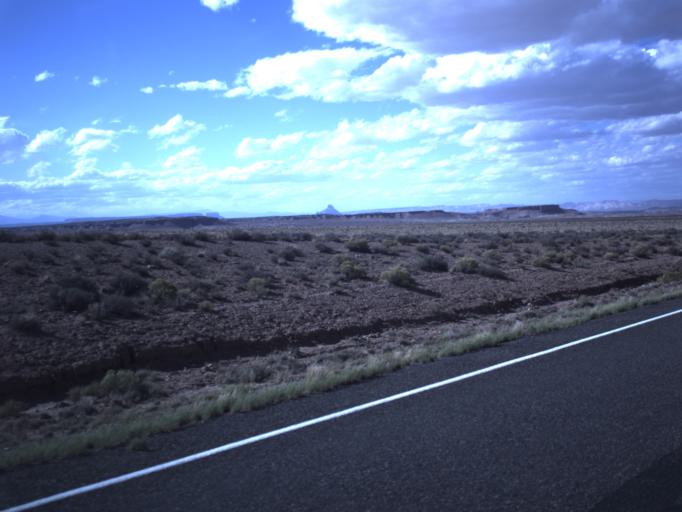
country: US
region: Utah
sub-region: Emery County
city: Ferron
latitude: 38.2846
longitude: -110.6637
